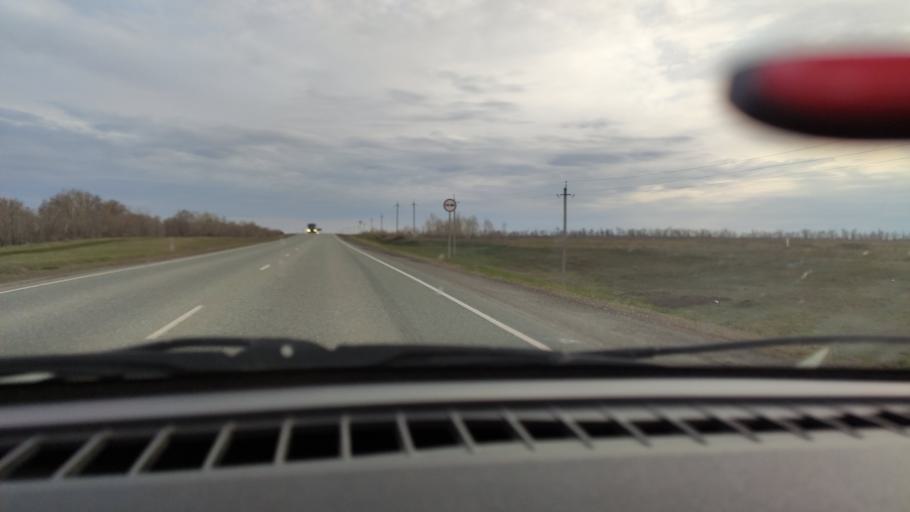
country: RU
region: Orenburg
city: Tatarskaya Kargala
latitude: 52.0053
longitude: 55.2006
